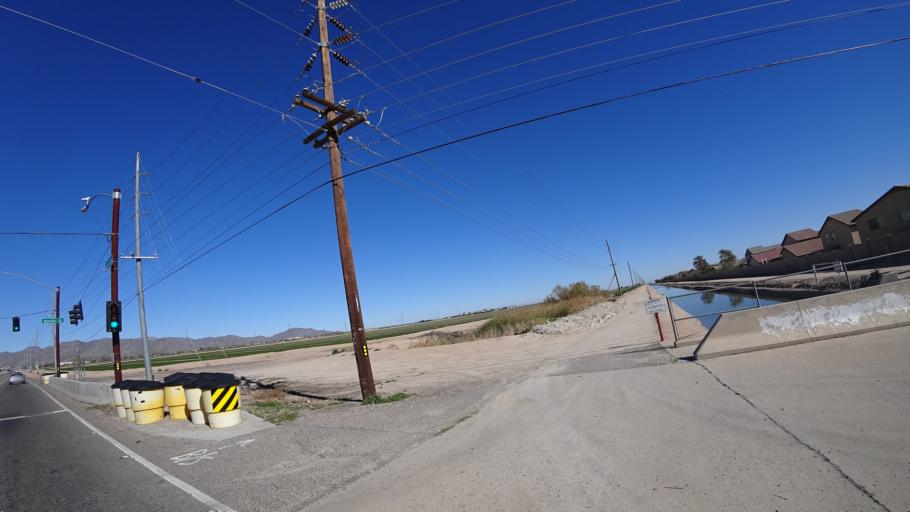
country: US
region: Arizona
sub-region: Maricopa County
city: Buckeye
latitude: 33.4125
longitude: -112.5909
